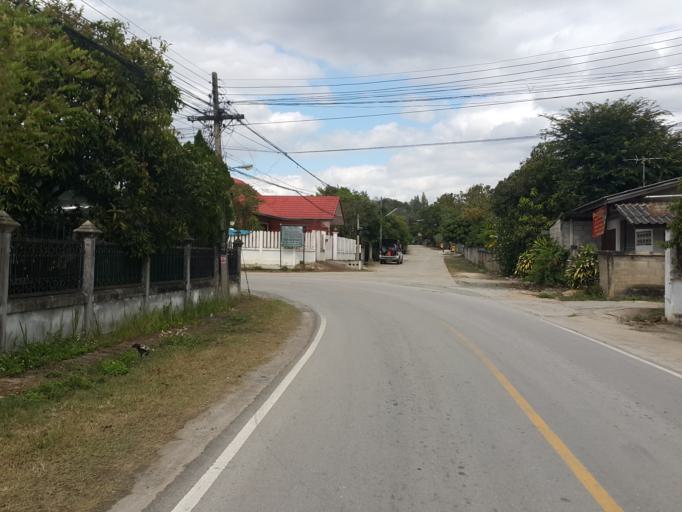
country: TH
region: Chiang Mai
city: San Sai
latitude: 18.8620
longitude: 99.1410
